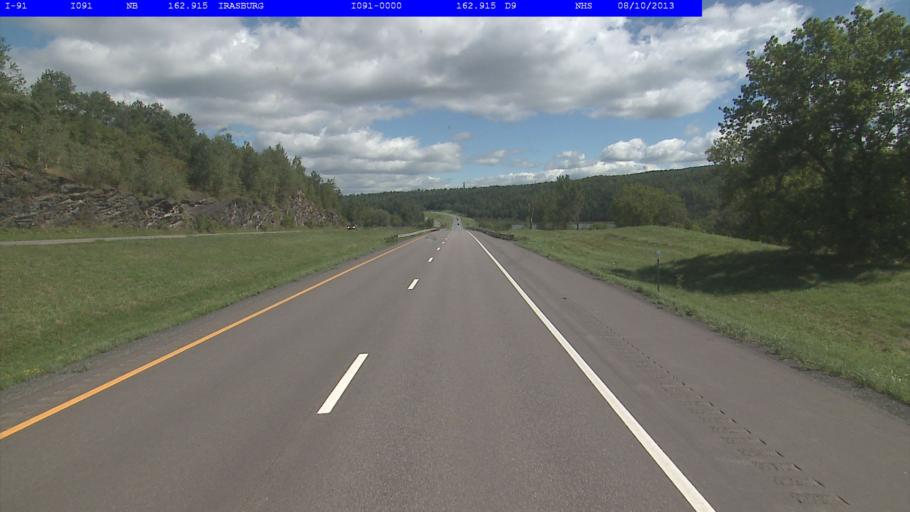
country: US
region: Vermont
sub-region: Orleans County
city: Newport
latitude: 44.8265
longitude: -72.2037
